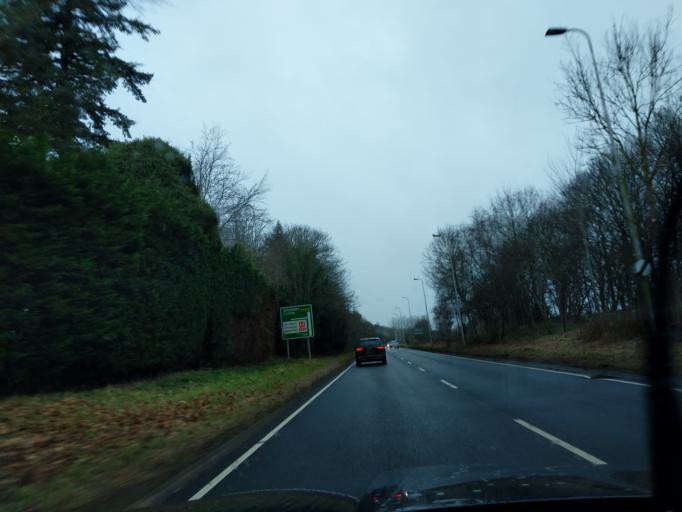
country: GB
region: Scotland
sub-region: The Scottish Borders
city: Melrose
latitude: 55.5967
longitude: -2.7337
